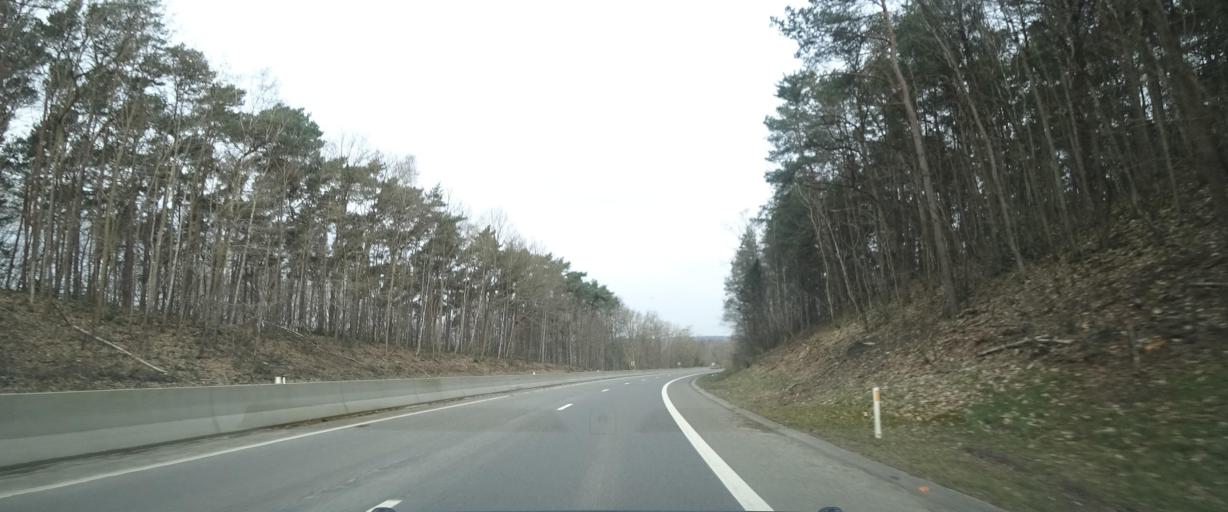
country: BE
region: Wallonia
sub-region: Province du Brabant Wallon
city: Ottignies
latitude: 50.6722
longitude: 4.5842
